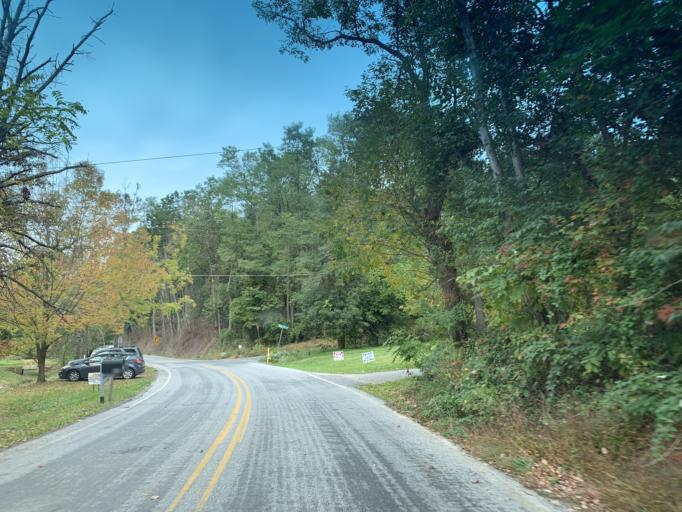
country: US
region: Pennsylvania
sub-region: York County
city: Stewartstown
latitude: 39.8160
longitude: -76.5202
